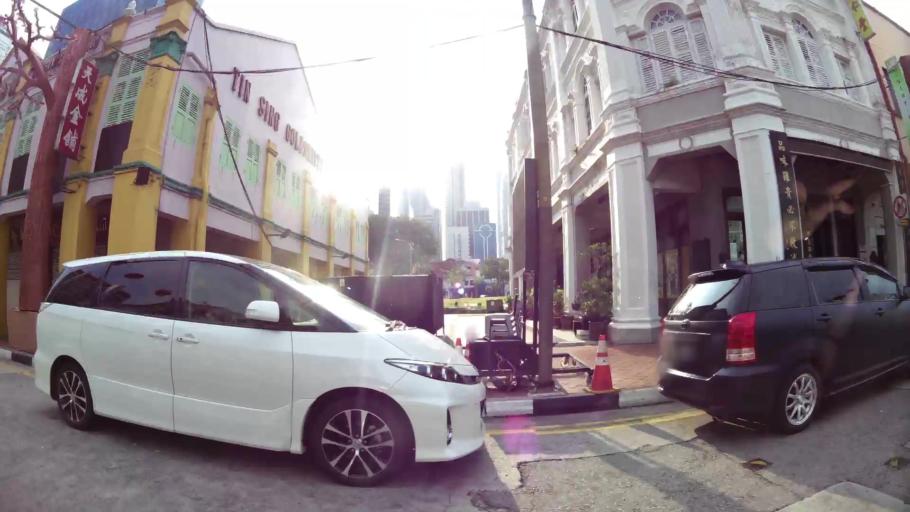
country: SG
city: Singapore
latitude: 1.2832
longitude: 103.8459
